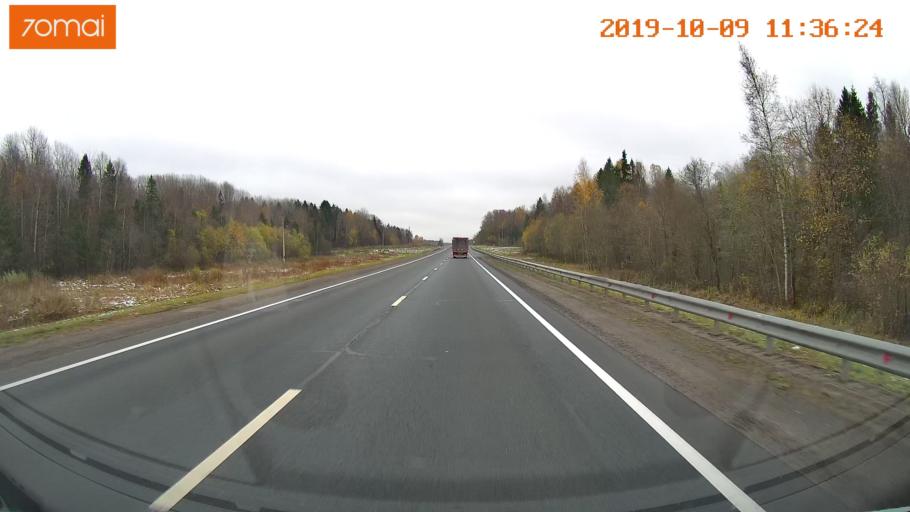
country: RU
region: Vologda
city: Gryazovets
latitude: 58.9912
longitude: 40.1363
